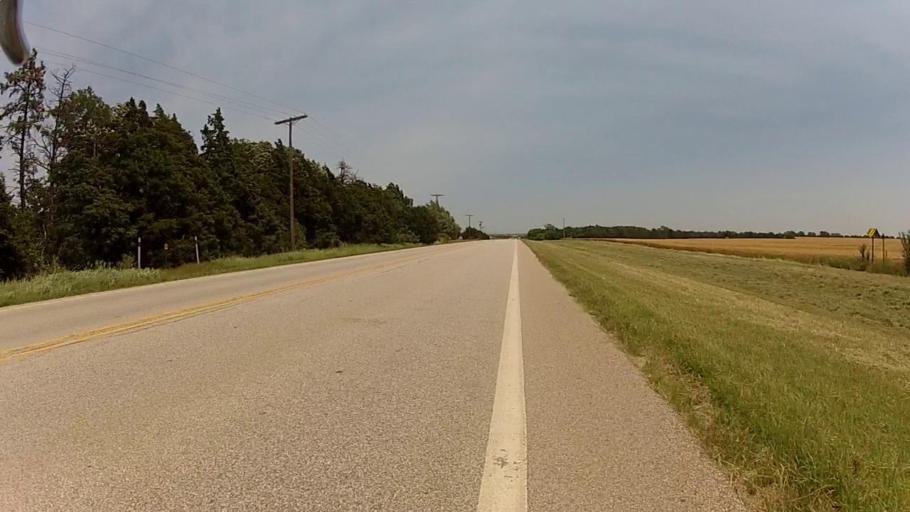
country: US
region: Kansas
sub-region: Cowley County
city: Arkansas City
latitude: 37.0565
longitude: -97.1590
